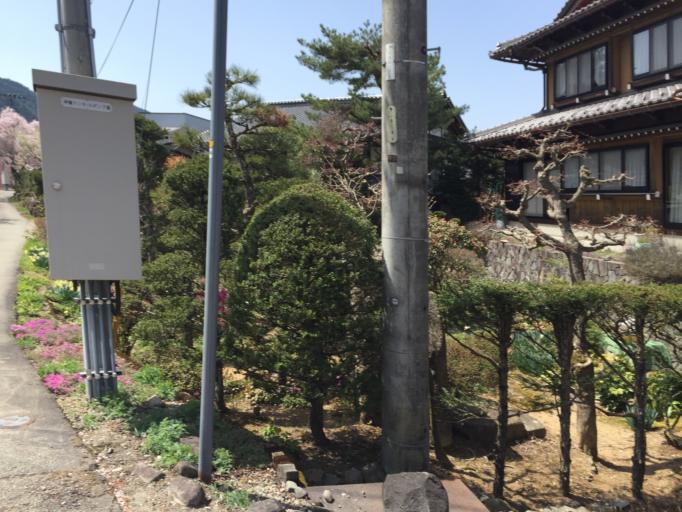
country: JP
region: Gifu
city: Takayama
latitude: 36.0864
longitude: 137.2505
